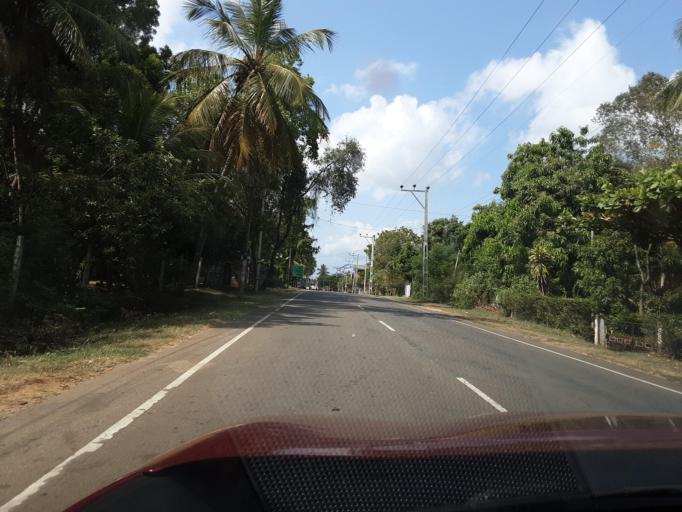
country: LK
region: Southern
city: Tangalla
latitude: 6.2956
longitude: 81.2362
